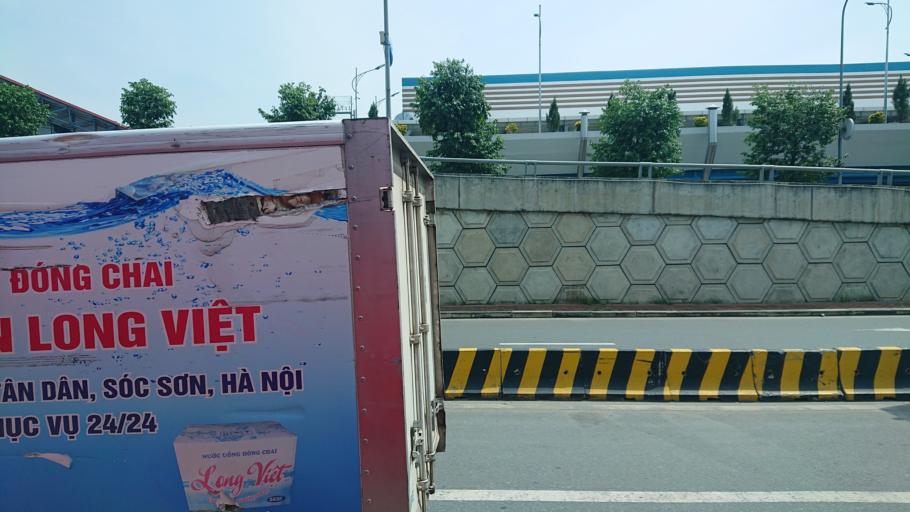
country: VN
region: Ha Noi
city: Soc Son
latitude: 21.2126
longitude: 105.8046
